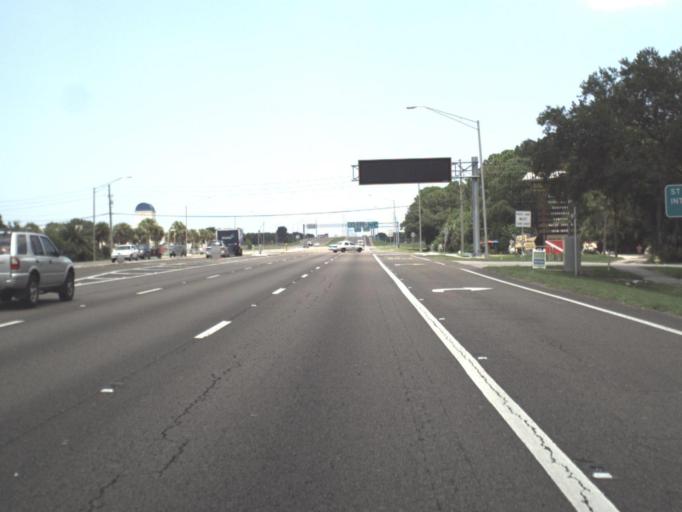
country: US
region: Florida
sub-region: Pinellas County
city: Pinellas Park
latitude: 27.8565
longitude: -82.6959
